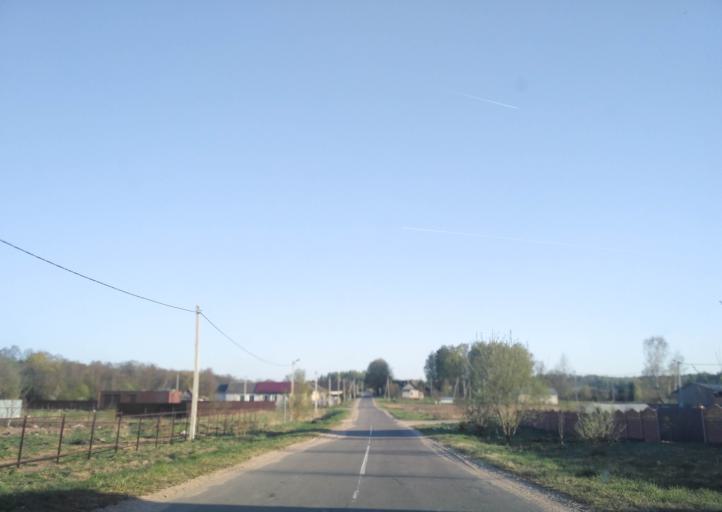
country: BY
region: Minsk
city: Pyatryshki
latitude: 54.1085
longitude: 27.1916
